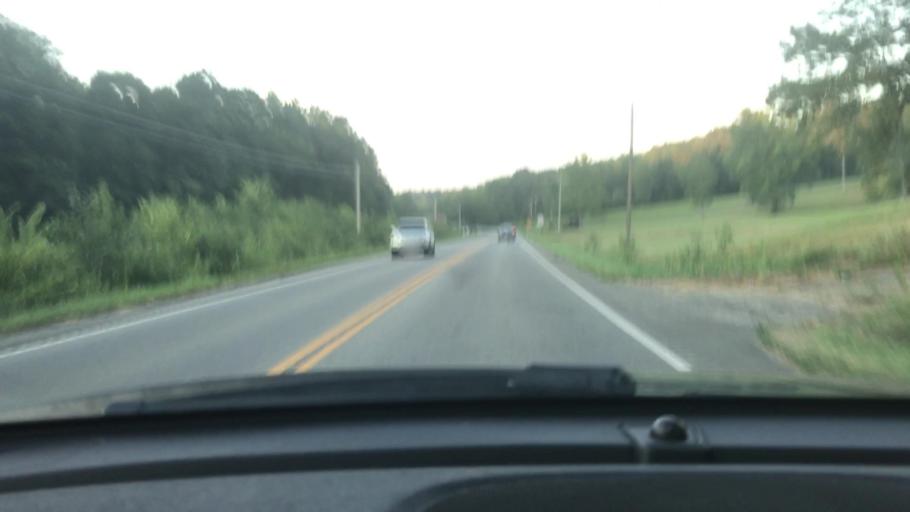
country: US
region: Tennessee
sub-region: Dickson County
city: Dickson
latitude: 36.1188
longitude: -87.3644
